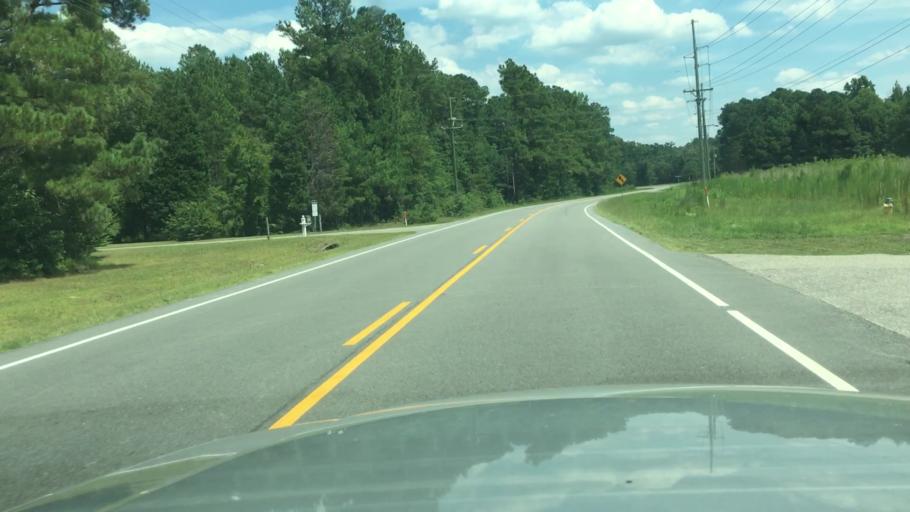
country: US
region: North Carolina
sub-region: Cumberland County
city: Hope Mills
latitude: 34.9495
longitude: -78.8861
